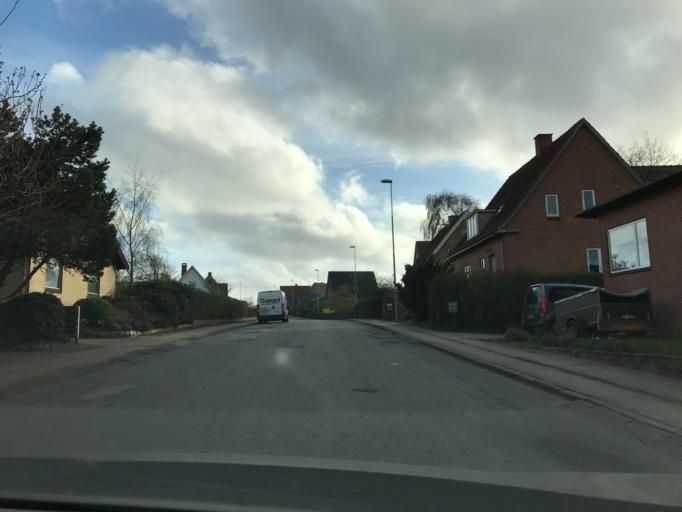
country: DK
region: Central Jutland
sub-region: Skive Kommune
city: Skive
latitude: 56.5715
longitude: 9.0144
